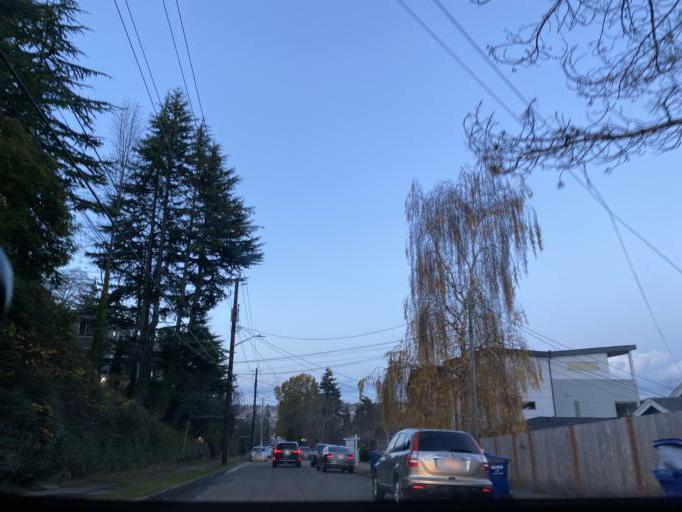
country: US
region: Washington
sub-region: King County
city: Seattle
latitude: 47.6511
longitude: -122.3860
